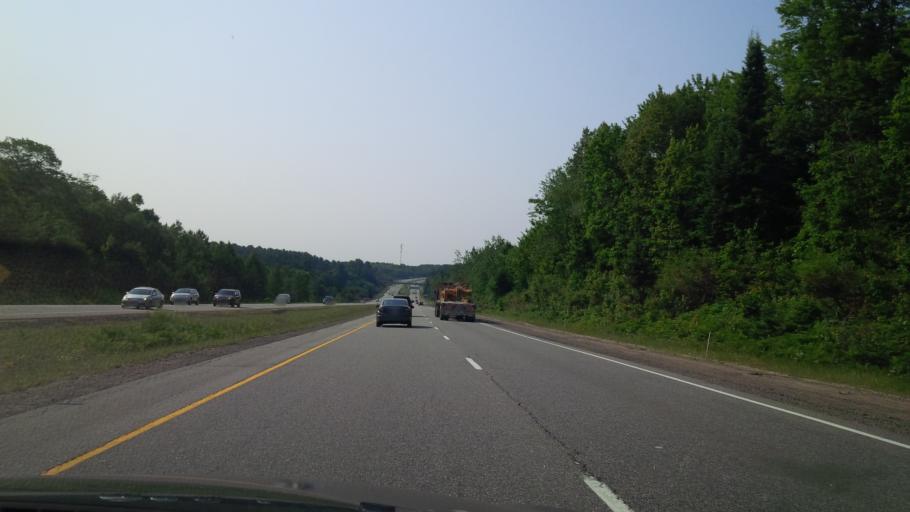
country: CA
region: Ontario
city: Bracebridge
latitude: 45.0954
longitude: -79.3045
